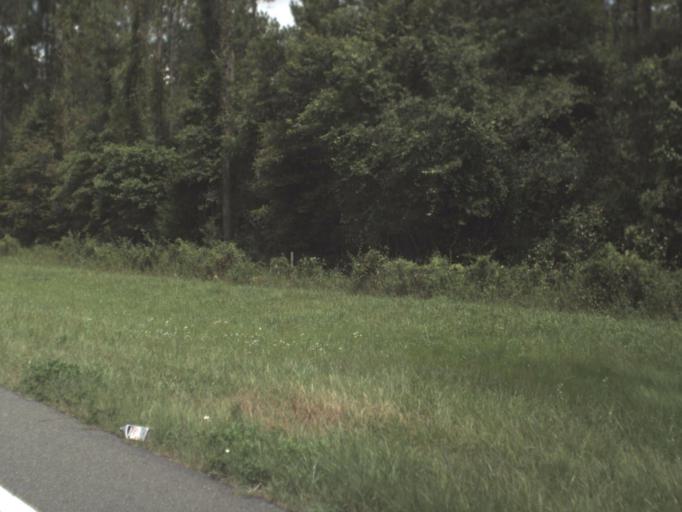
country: US
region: Florida
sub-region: Alachua County
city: Alachua
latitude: 29.8223
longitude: -82.4378
